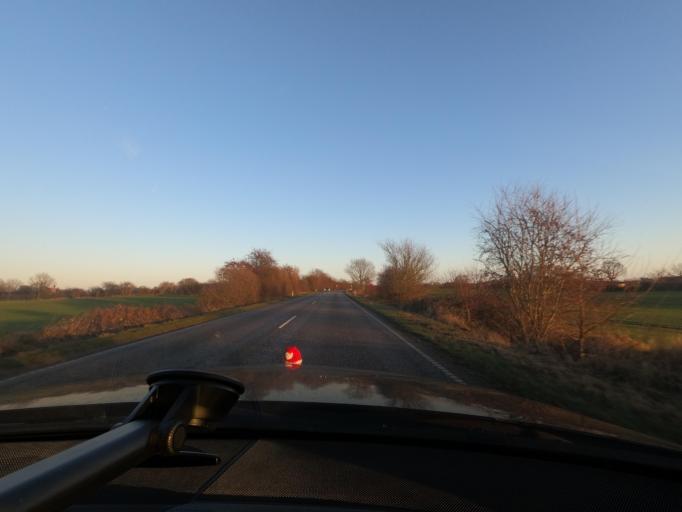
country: DK
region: South Denmark
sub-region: Sonderborg Kommune
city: Horuphav
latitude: 54.9216
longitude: 9.8899
